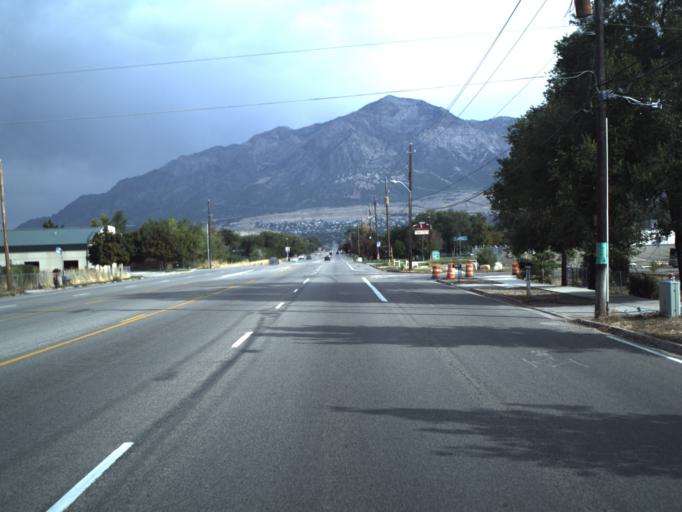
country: US
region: Utah
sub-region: Weber County
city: Harrisville
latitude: 41.2792
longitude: -111.9692
